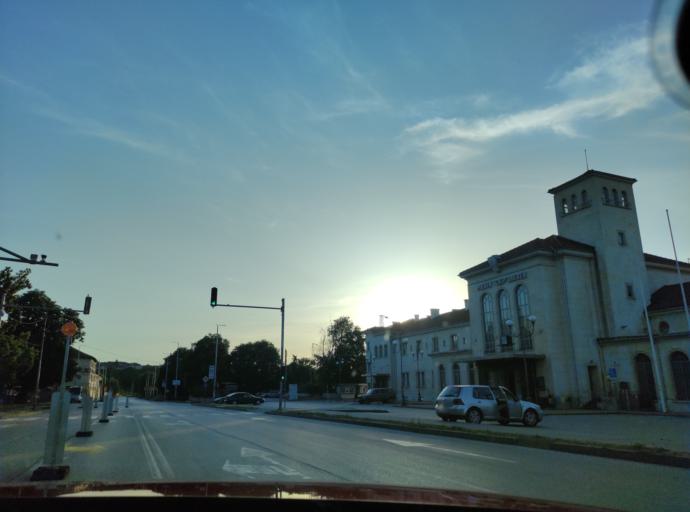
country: BG
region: Pleven
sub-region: Obshtina Pleven
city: Pleven
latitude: 43.4204
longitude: 24.6150
